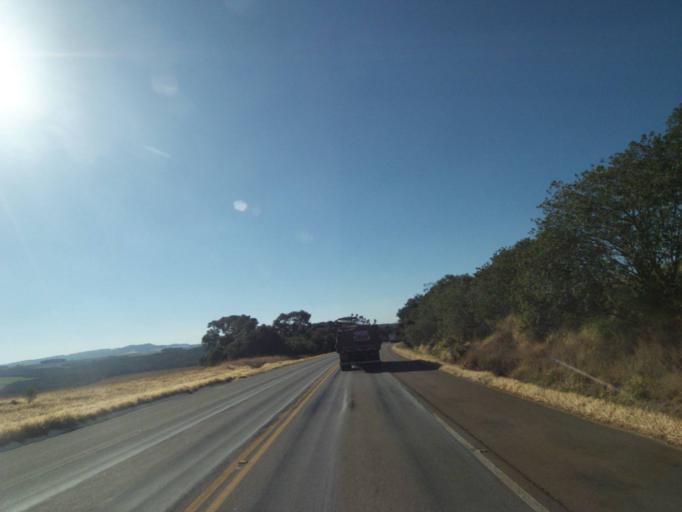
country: BR
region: Parana
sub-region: Tibagi
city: Tibagi
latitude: -24.6682
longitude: -50.4531
